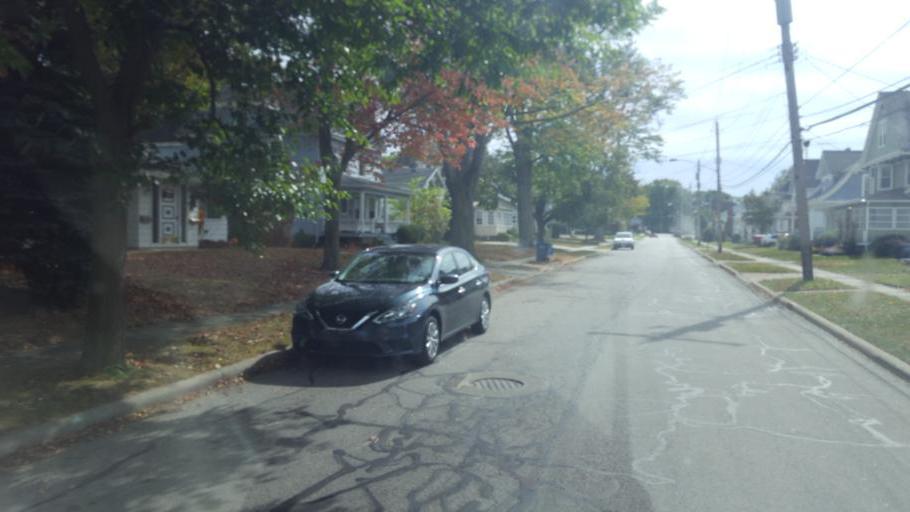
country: US
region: Ohio
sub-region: Lorain County
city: Amherst
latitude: 41.4000
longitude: -82.2214
